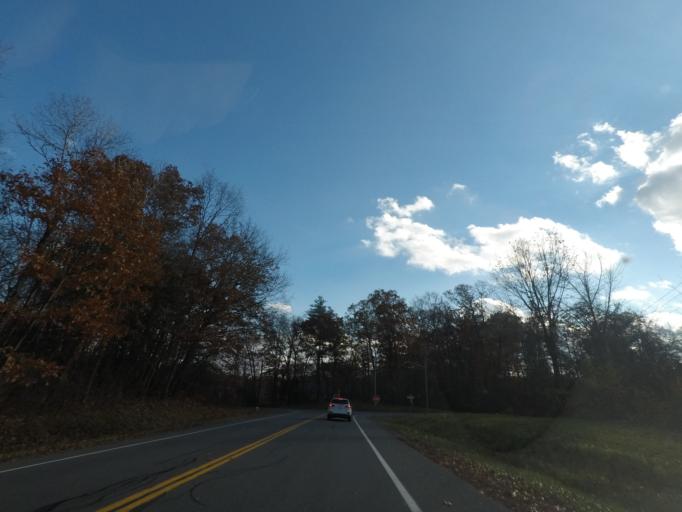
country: US
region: New York
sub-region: Schenectady County
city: Niskayuna
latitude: 42.7970
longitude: -73.8552
